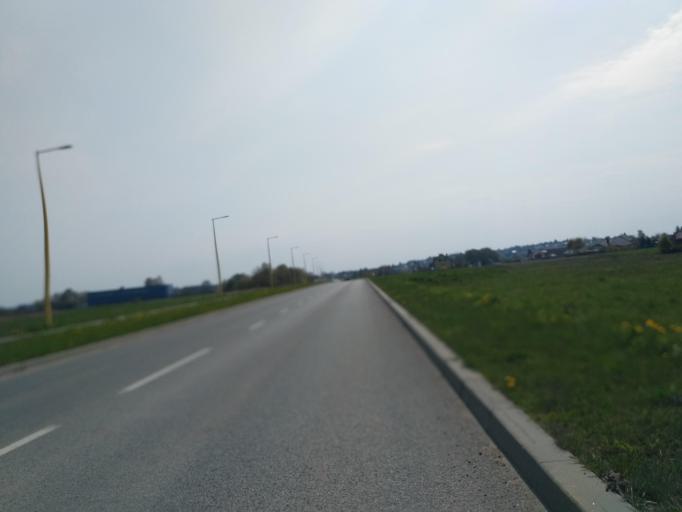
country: PL
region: Subcarpathian Voivodeship
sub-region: Krosno
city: Krosno
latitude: 49.6745
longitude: 21.7394
